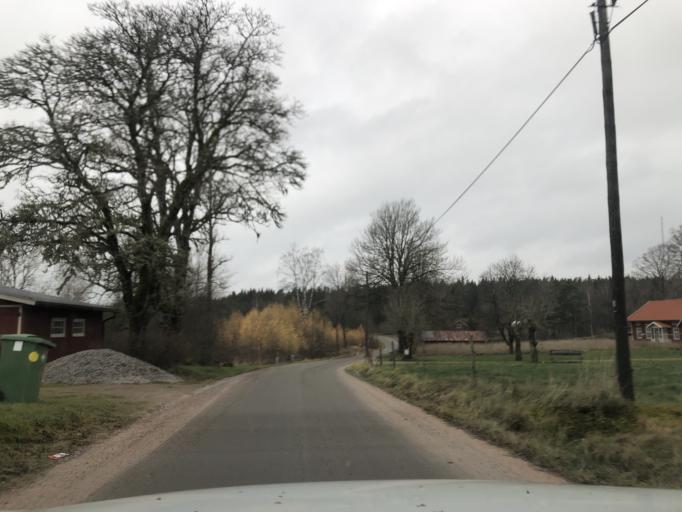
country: SE
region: Vaestra Goetaland
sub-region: Ulricehamns Kommun
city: Ulricehamn
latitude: 57.8629
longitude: 13.5713
